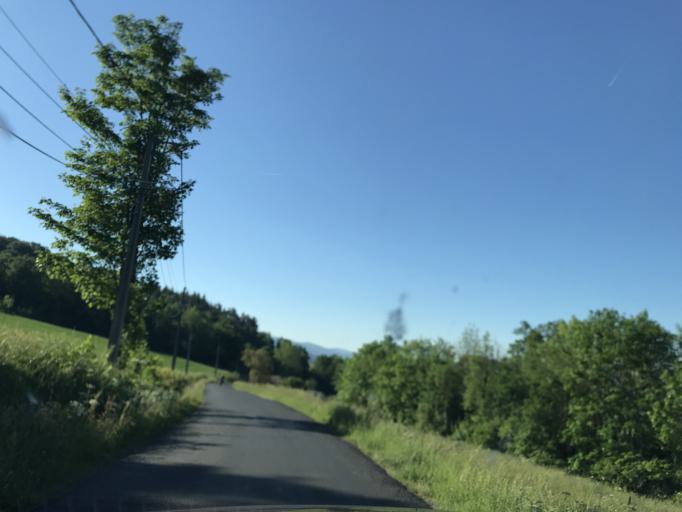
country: FR
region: Auvergne
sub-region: Departement du Puy-de-Dome
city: Job
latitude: 45.6729
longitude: 3.7015
